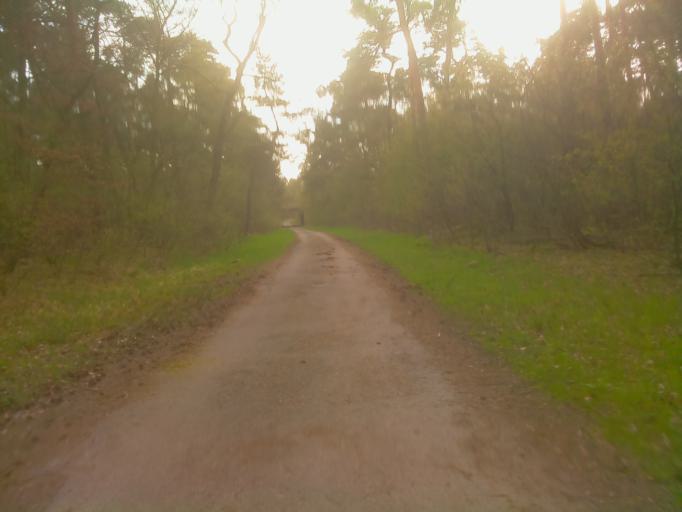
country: DE
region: Hesse
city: Lampertheim
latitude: 49.5570
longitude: 8.4914
